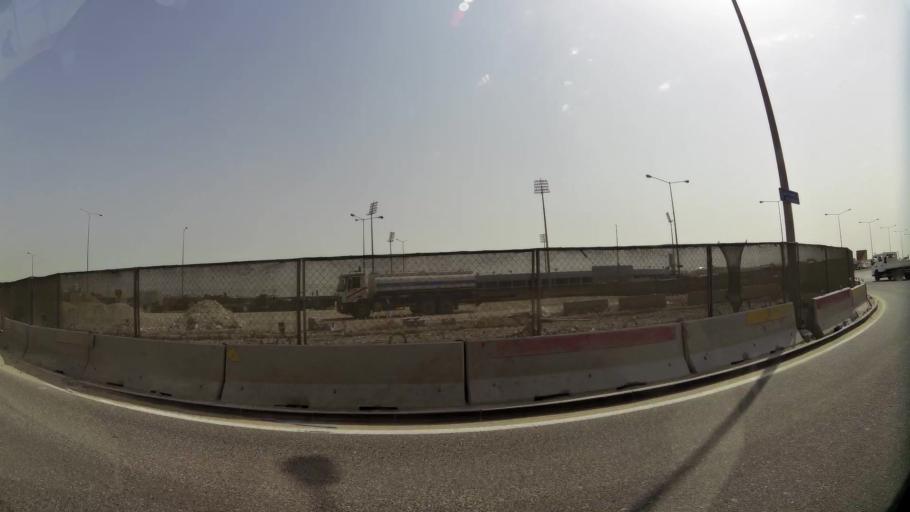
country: QA
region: Al Wakrah
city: Al Wukayr
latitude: 25.1891
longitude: 51.4572
